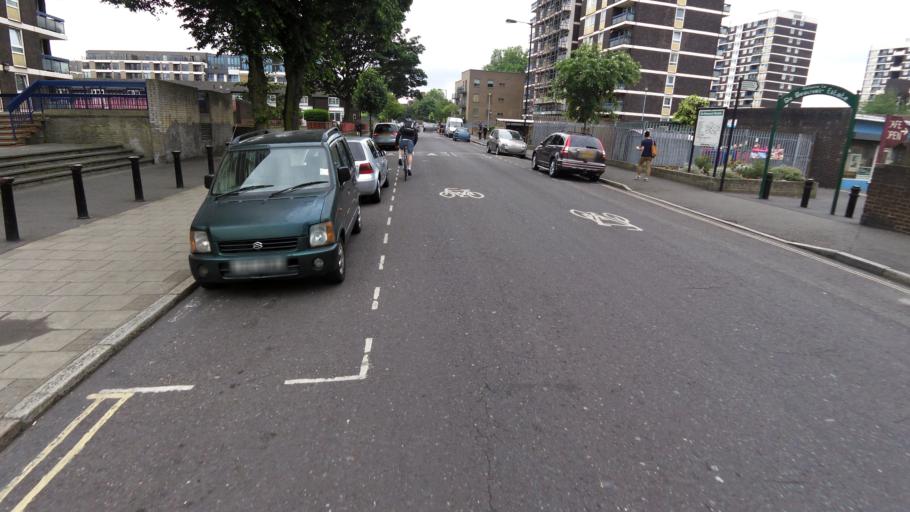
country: GB
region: England
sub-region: Greater London
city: Islington
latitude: 51.5389
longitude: -0.0812
